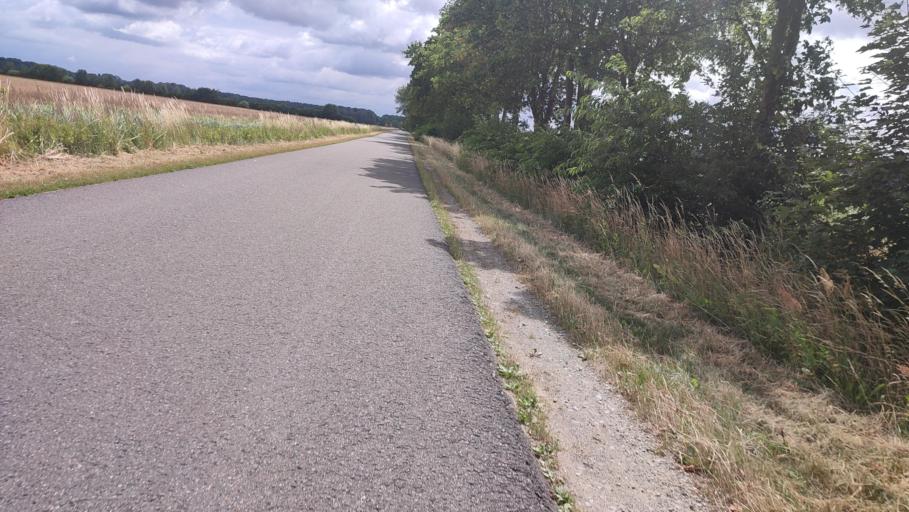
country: DE
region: Lower Saxony
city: Hitzacker
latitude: 53.1988
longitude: 11.1043
